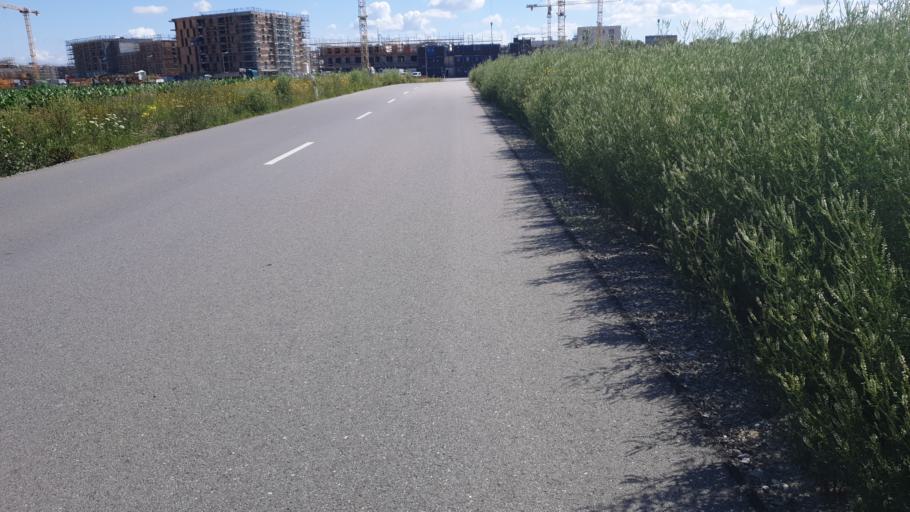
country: DE
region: Bavaria
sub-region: Upper Bavaria
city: Germering
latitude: 48.1471
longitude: 11.4025
